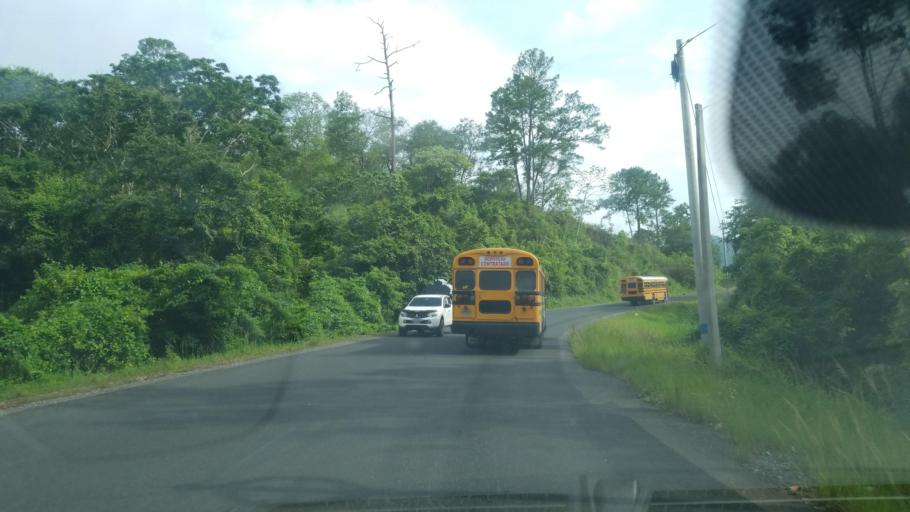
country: HN
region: Santa Barbara
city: Petoa
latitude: 15.2036
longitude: -88.2695
